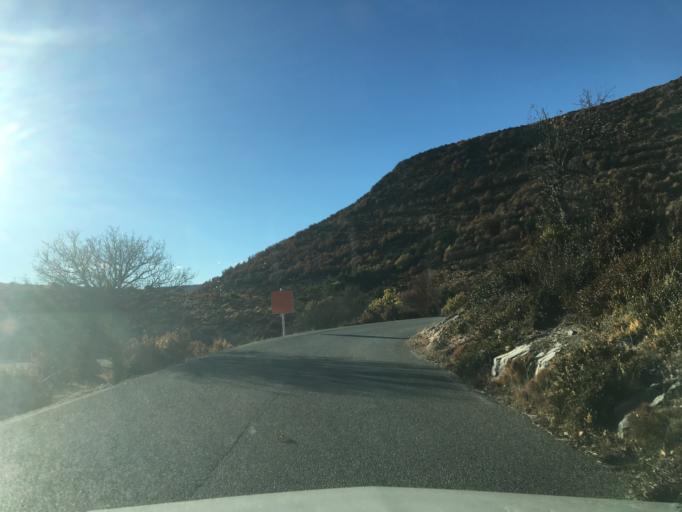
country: FR
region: Provence-Alpes-Cote d'Azur
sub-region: Departement des Alpes-de-Haute-Provence
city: Castellane
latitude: 43.7526
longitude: 6.4061
